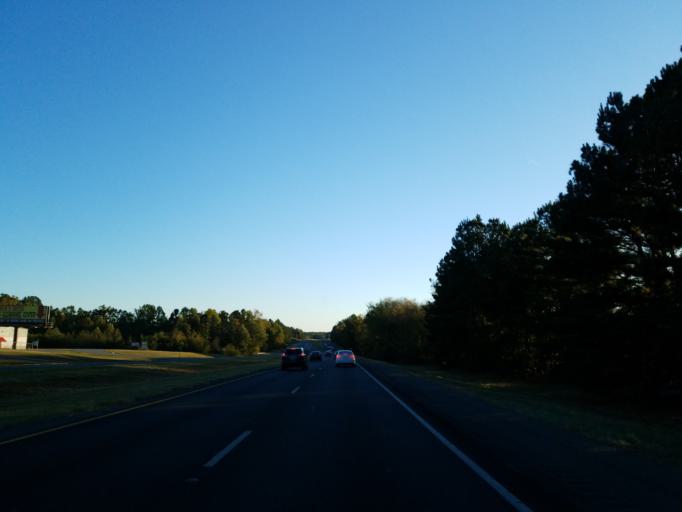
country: US
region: Georgia
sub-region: Dawson County
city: Dawsonville
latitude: 34.3226
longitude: -84.0604
